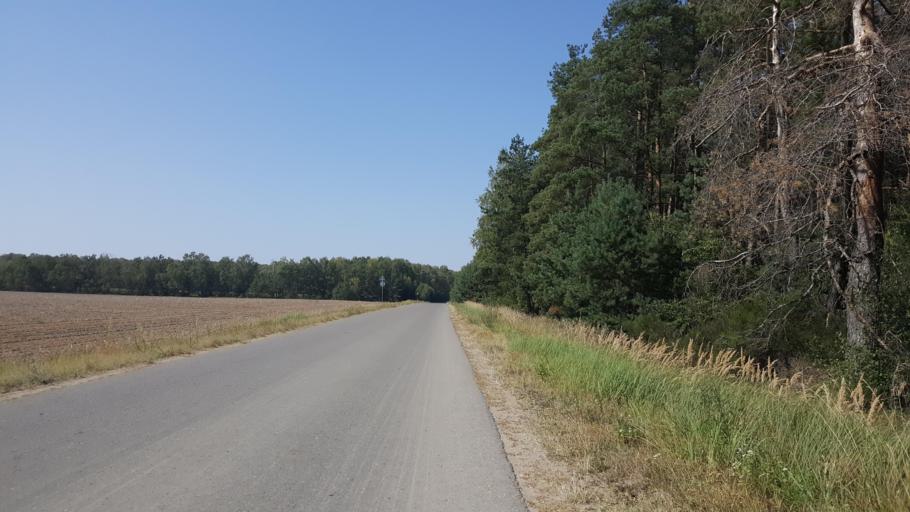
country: BY
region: Brest
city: Vysokaye
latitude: 52.4281
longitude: 23.4524
